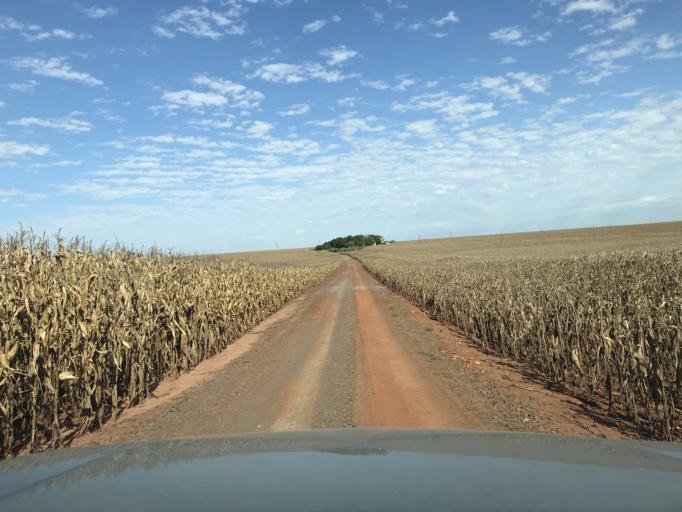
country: BR
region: Parana
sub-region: Palotina
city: Palotina
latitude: -24.1707
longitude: -53.7580
